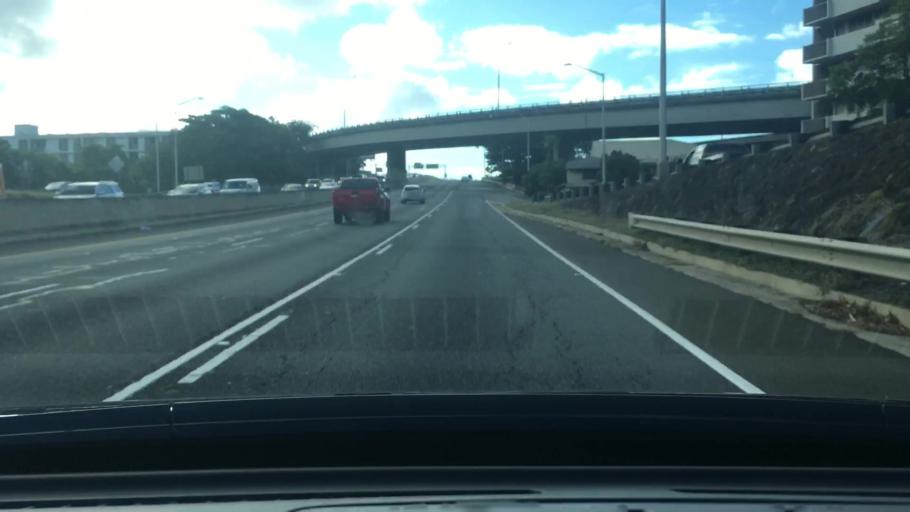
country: US
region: Hawaii
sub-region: Honolulu County
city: Honolulu
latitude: 21.2902
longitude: -157.8168
